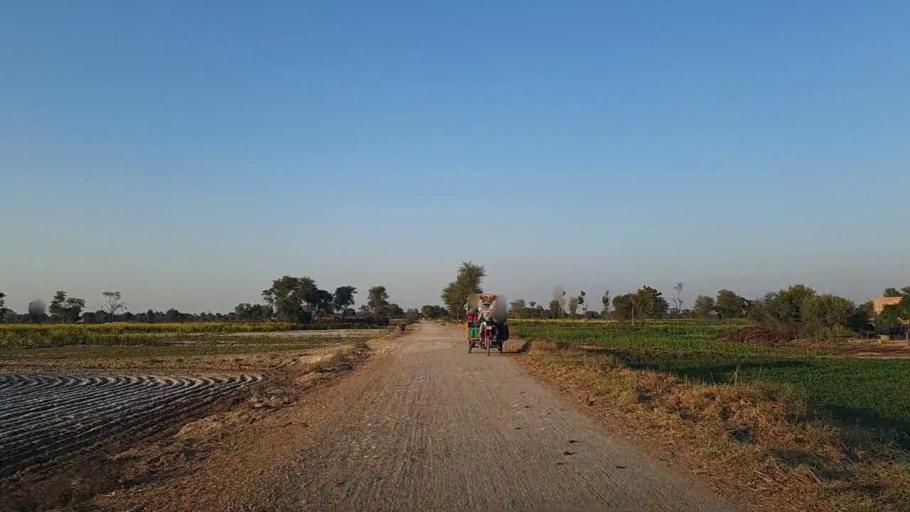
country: PK
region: Sindh
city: Nawabshah
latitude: 26.2329
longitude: 68.3381
